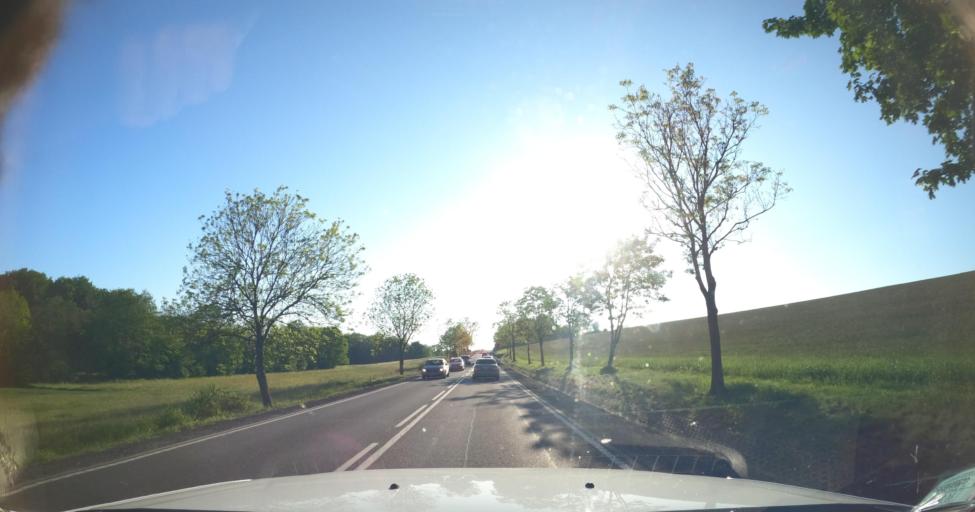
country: PL
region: Pomeranian Voivodeship
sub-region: Powiat kartuski
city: Zukowo
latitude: 54.3391
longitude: 18.3863
